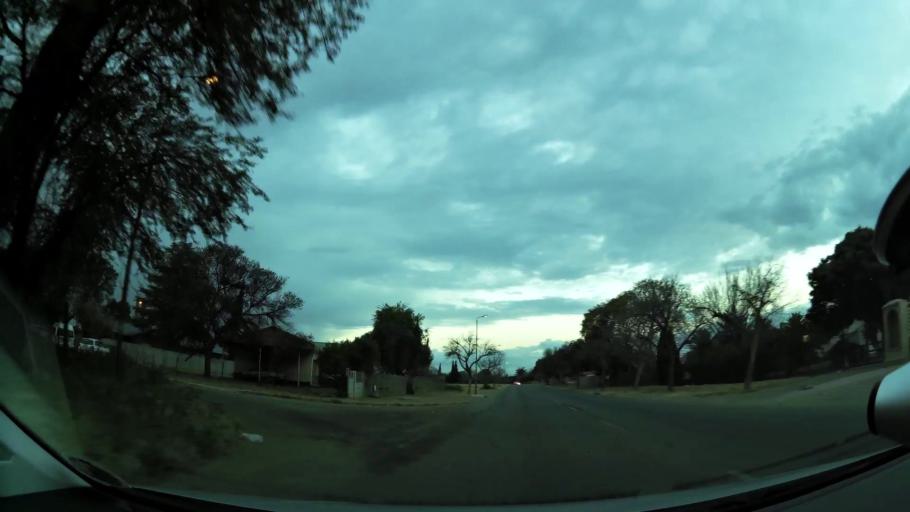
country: ZA
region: Orange Free State
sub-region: Lejweleputswa District Municipality
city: Welkom
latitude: -27.9786
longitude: 26.7481
